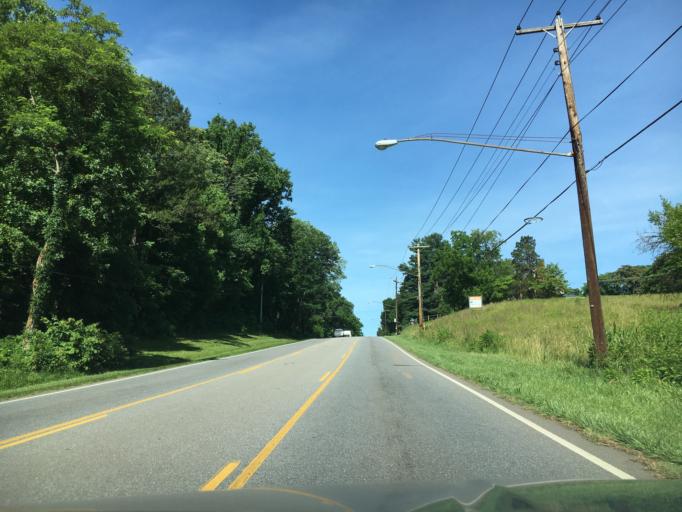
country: US
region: Virginia
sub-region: City of Lynchburg
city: West Lynchburg
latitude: 37.4020
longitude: -79.1935
